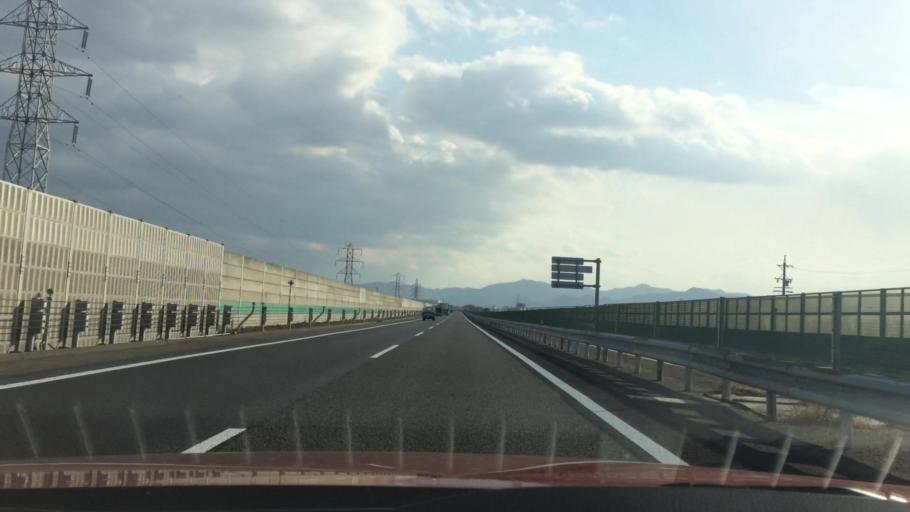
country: JP
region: Nagano
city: Matsumoto
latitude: 36.1836
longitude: 137.9391
